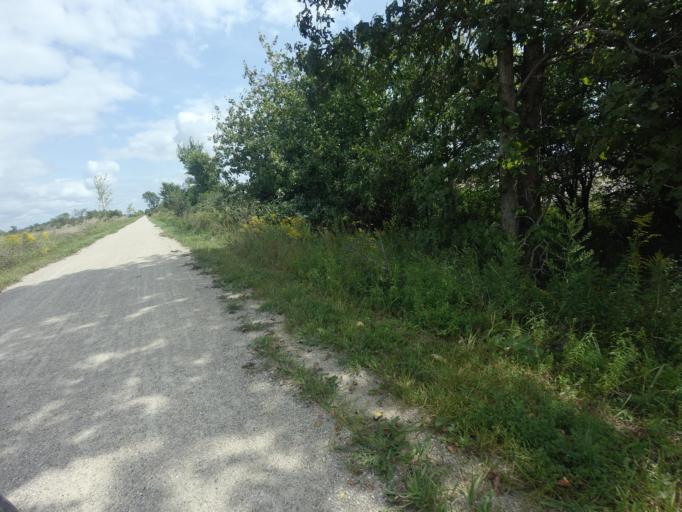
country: CA
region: Ontario
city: North Perth
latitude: 43.5744
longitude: -80.8315
